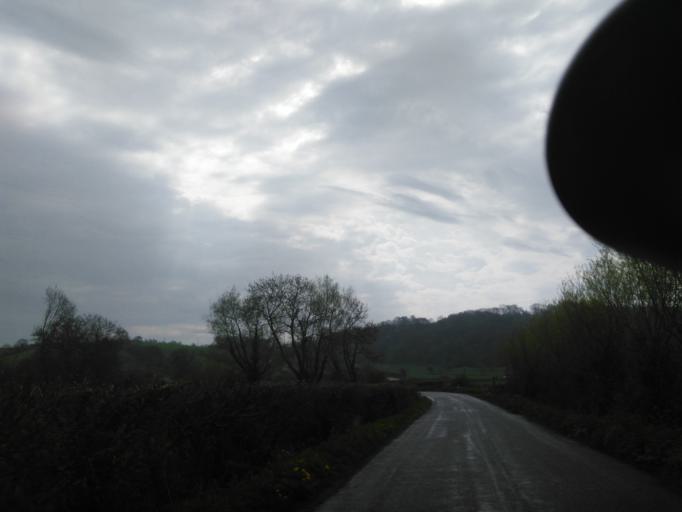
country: GB
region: England
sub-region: Somerset
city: Langport
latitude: 51.0887
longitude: -2.8207
